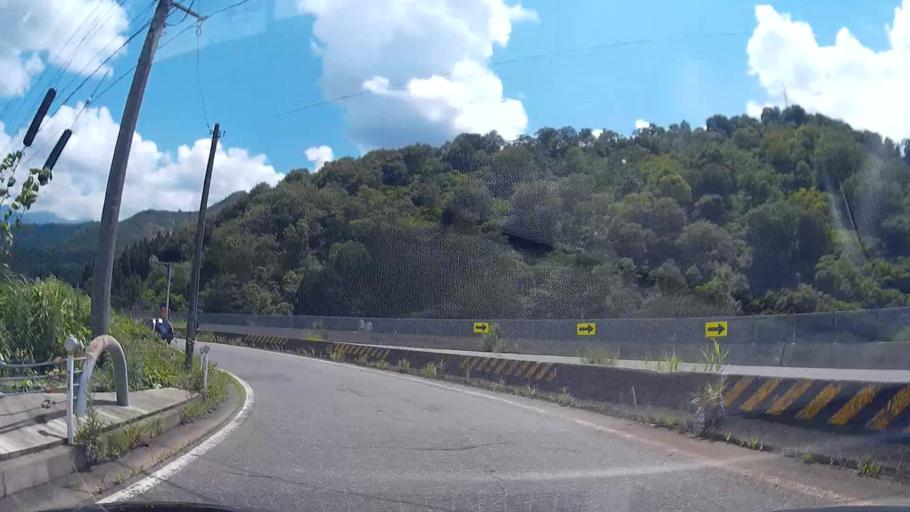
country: JP
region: Niigata
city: Shiozawa
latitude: 36.9212
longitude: 138.8124
